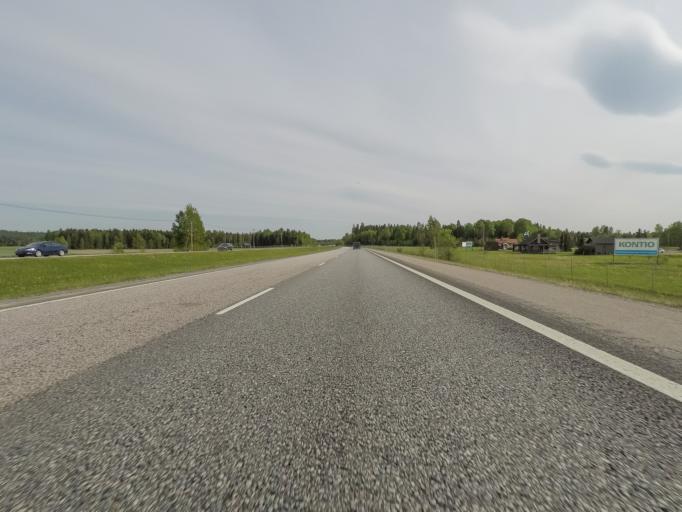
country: FI
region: Uusimaa
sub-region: Helsinki
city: Nurmijaervi
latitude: 60.4806
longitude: 24.8488
